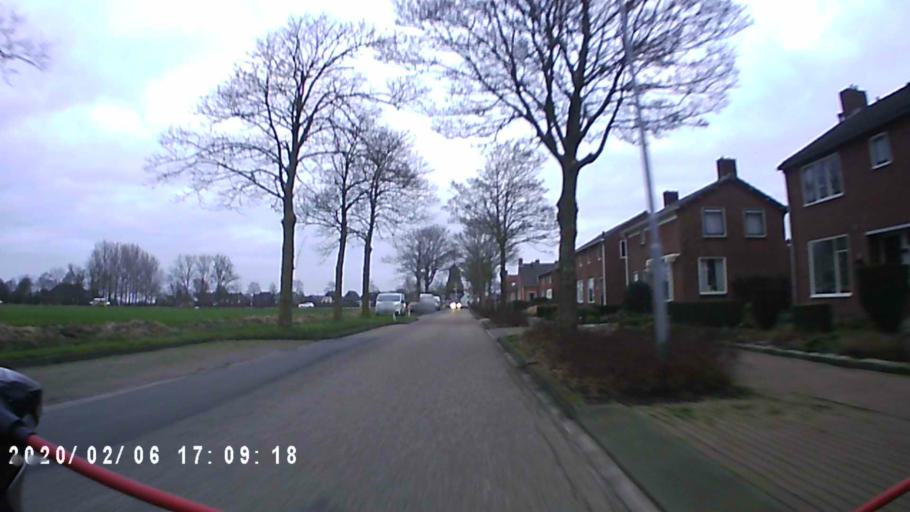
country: NL
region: Groningen
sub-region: Gemeente Winsum
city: Winsum
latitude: 53.2755
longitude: 6.5324
